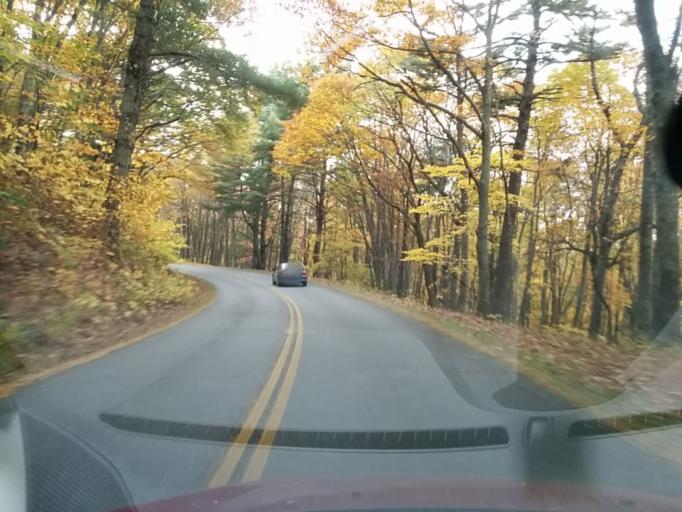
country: US
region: Virginia
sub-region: City of Buena Vista
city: Buena Vista
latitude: 37.8089
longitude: -79.1814
